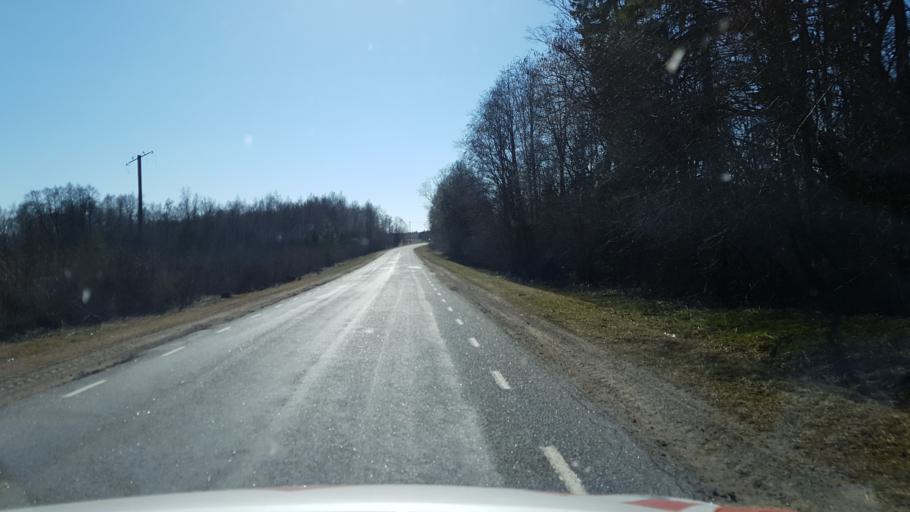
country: EE
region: Laeaene-Virumaa
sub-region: Tamsalu vald
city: Tamsalu
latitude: 59.0543
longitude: 26.0980
